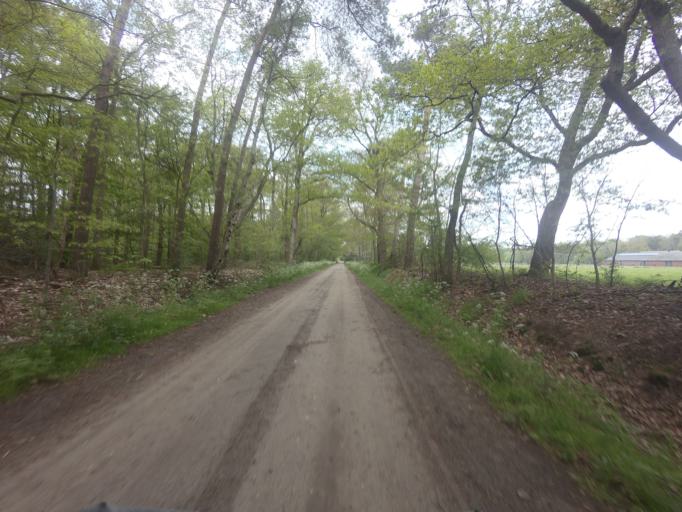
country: NL
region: Overijssel
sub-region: Gemeente Hof van Twente
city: Delden
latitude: 52.2454
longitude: 6.7217
